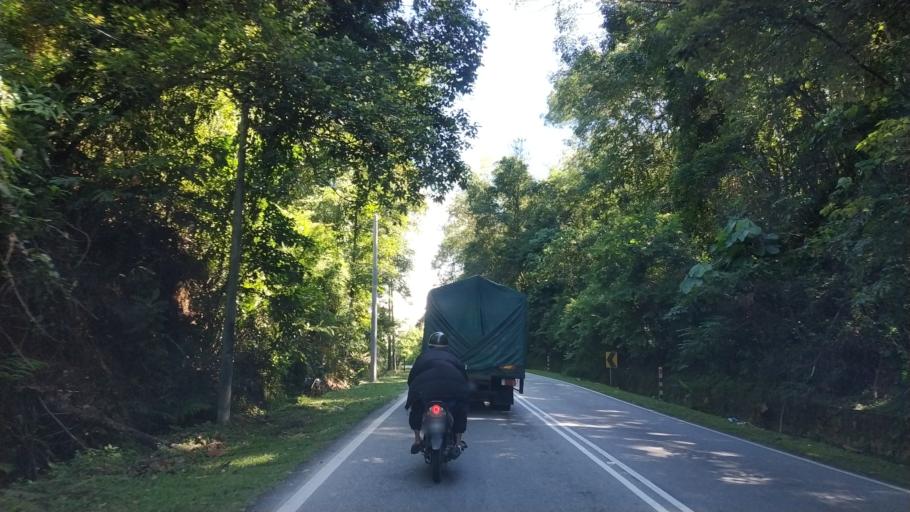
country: MY
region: Kedah
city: Kulim
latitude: 5.3284
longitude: 100.5325
